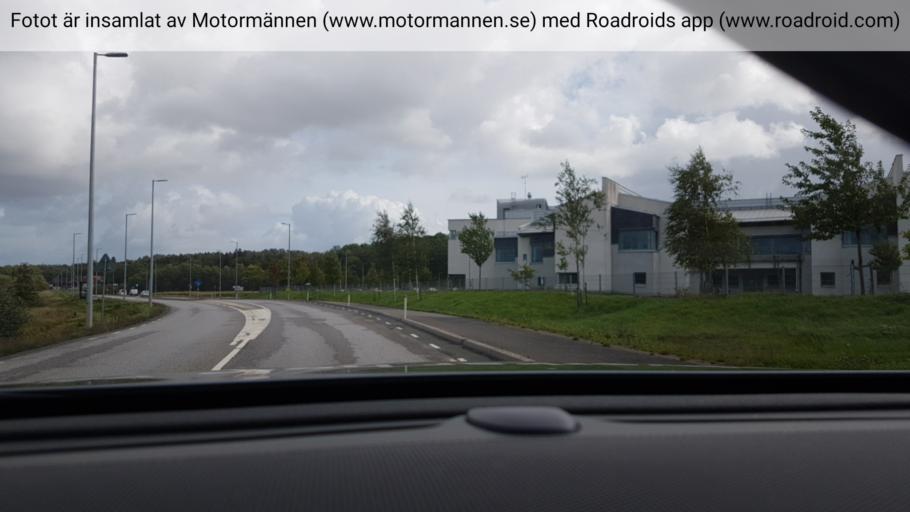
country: SE
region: Vaestra Goetaland
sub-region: Goteborg
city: Rannebergen
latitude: 57.7909
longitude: 12.1158
